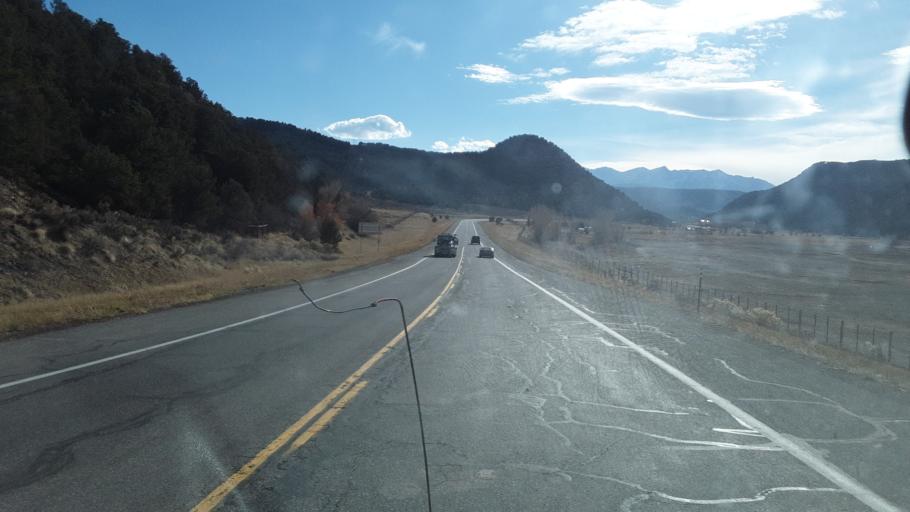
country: US
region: Colorado
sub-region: Ouray County
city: Ouray
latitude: 38.2058
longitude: -107.7328
